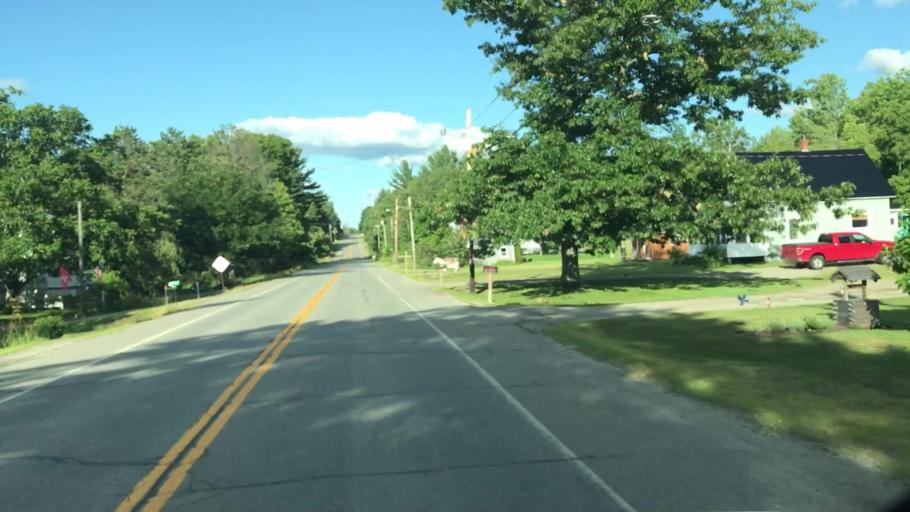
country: US
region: Maine
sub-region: Penobscot County
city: Lincoln
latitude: 45.3589
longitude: -68.2803
